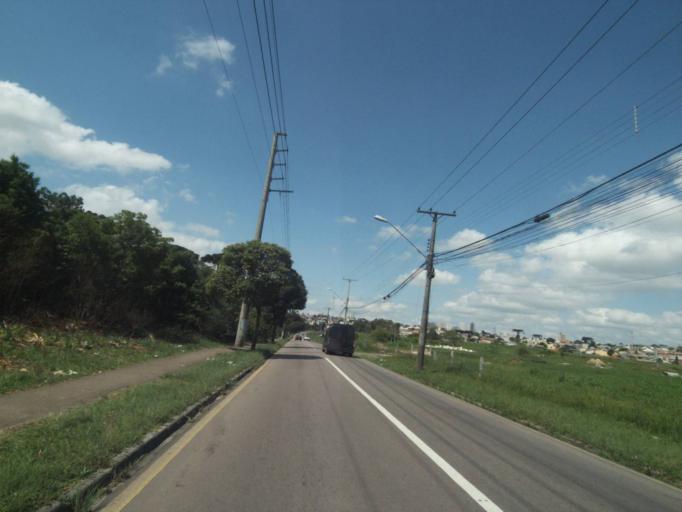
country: BR
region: Parana
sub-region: Curitiba
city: Curitiba
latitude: -25.5152
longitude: -49.3151
